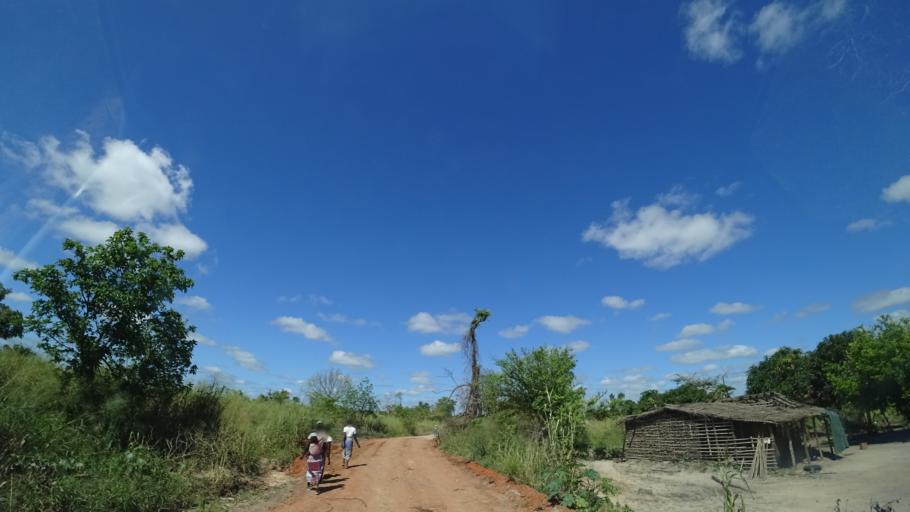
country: MZ
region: Sofala
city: Dondo
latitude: -19.2742
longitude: 34.6804
